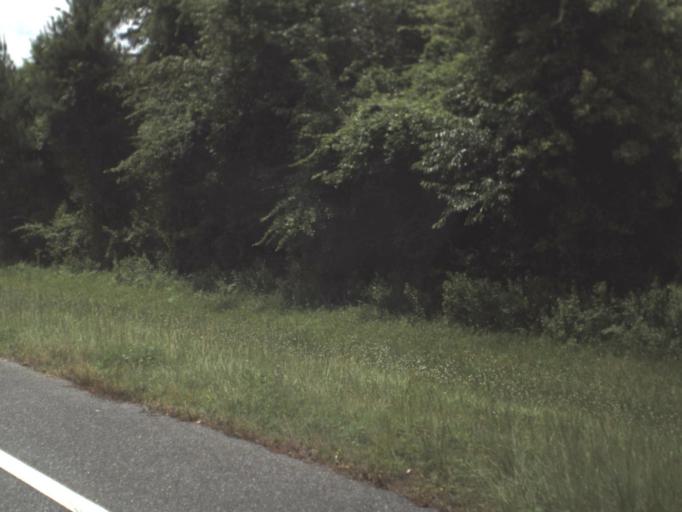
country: US
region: Florida
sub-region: Columbia County
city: Watertown
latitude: 30.1446
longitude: -82.5440
